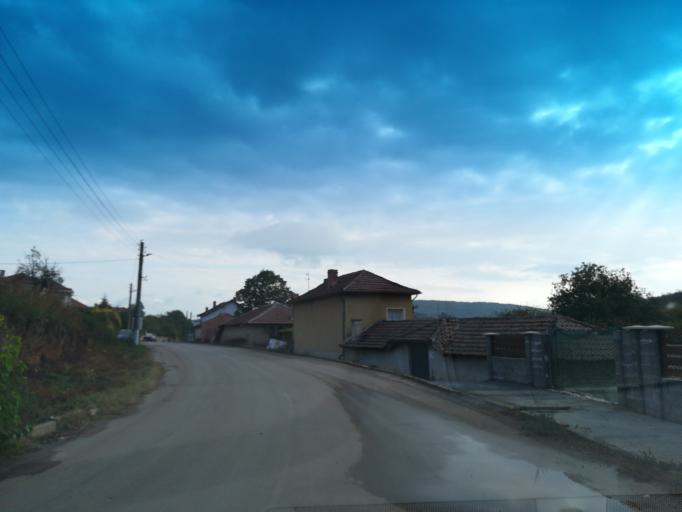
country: BG
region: Stara Zagora
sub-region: Obshtina Nikolaevo
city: Elkhovo
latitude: 42.3408
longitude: 25.4002
